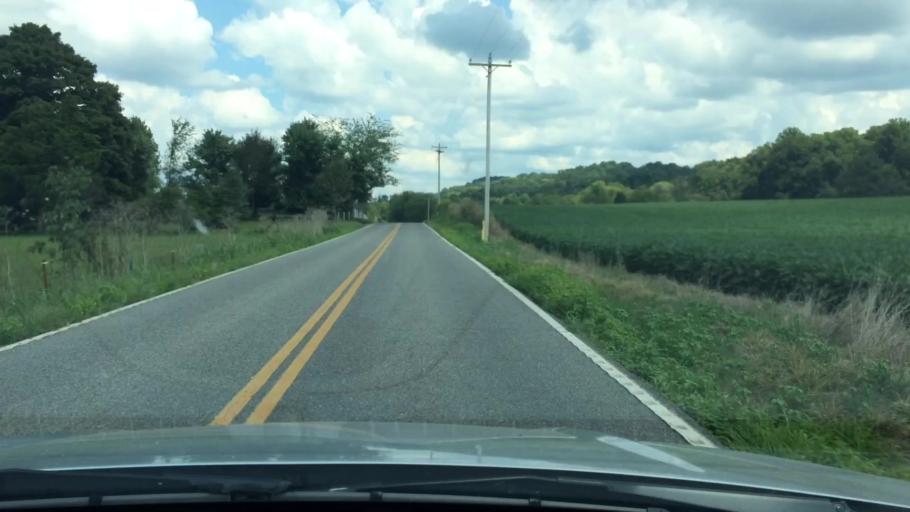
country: US
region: Tennessee
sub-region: McMinn County
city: Englewood
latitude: 35.5015
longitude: -84.4928
